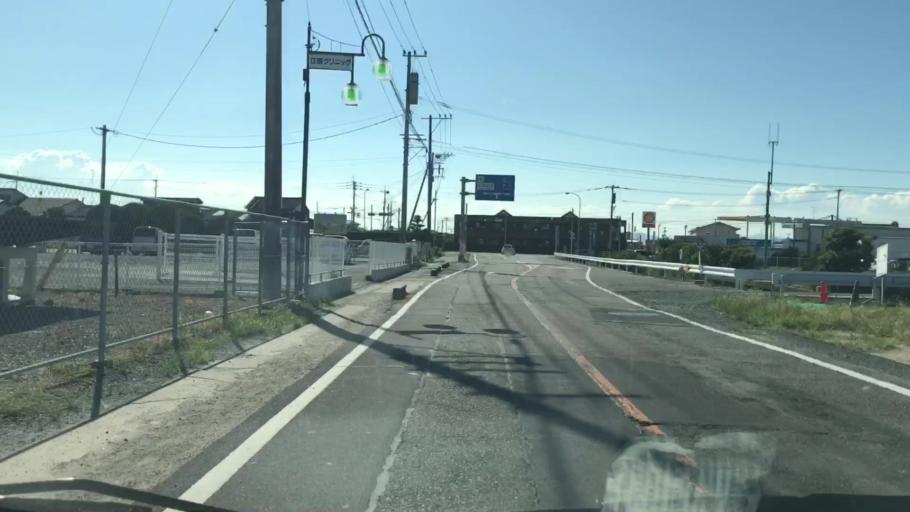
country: JP
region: Saga Prefecture
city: Okawa
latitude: 33.1917
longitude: 130.3169
